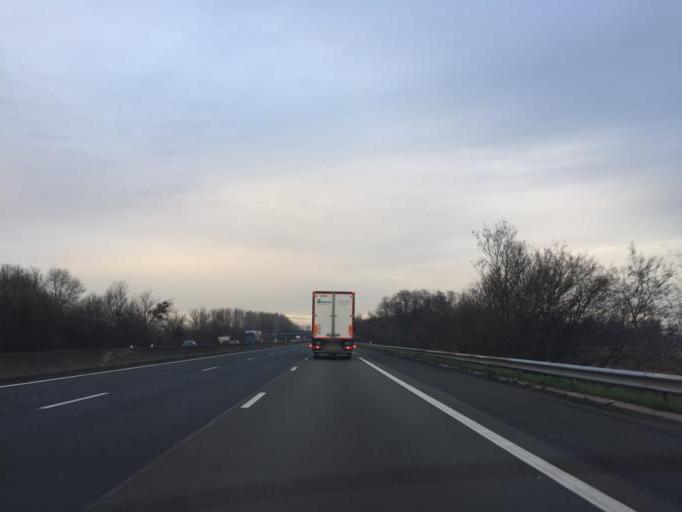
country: FR
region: Bourgogne
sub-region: Departement de Saone-et-Loire
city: Romaneche-Thorins
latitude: 46.1660
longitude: 4.7707
